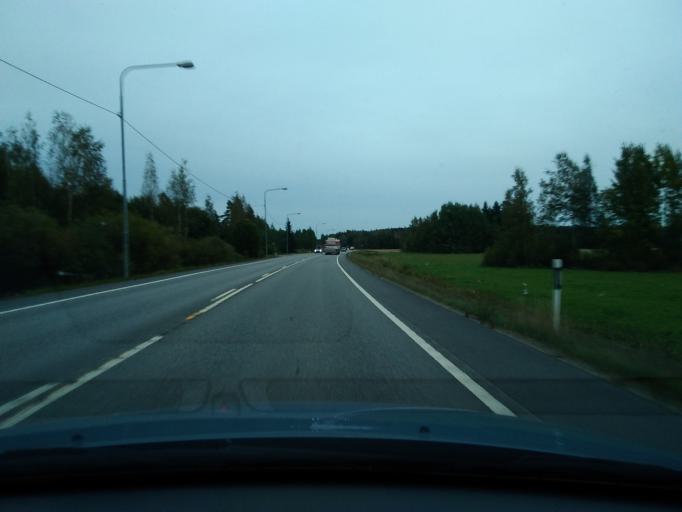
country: FI
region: Uusimaa
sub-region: Helsinki
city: Maentsaelae
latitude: 60.6198
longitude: 25.3150
